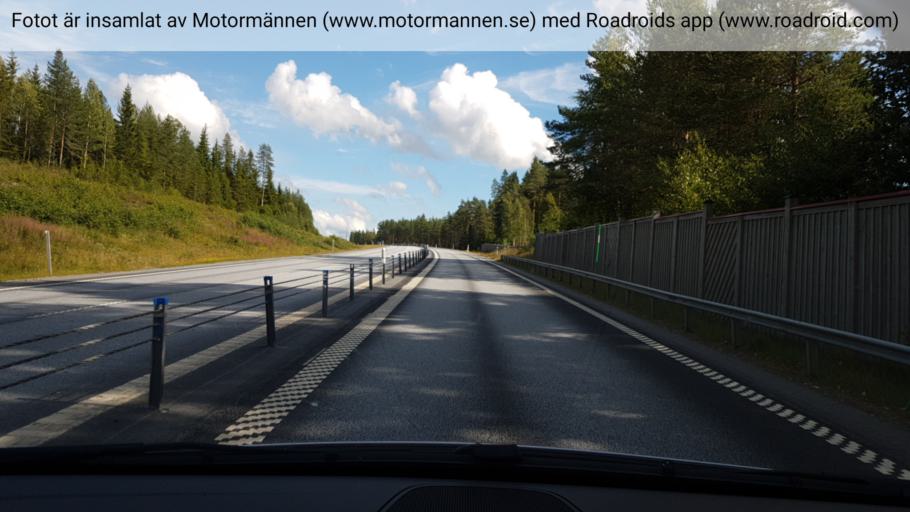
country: SE
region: Vaesterbotten
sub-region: Vannas Kommun
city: Vannasby
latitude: 63.8946
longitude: 19.9287
